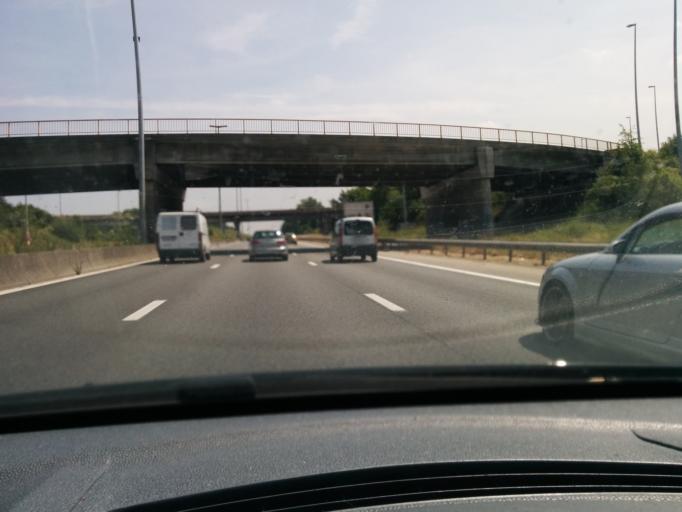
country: BE
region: Flanders
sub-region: Provincie Oost-Vlaanderen
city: Melle
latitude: 50.9755
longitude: 3.8319
